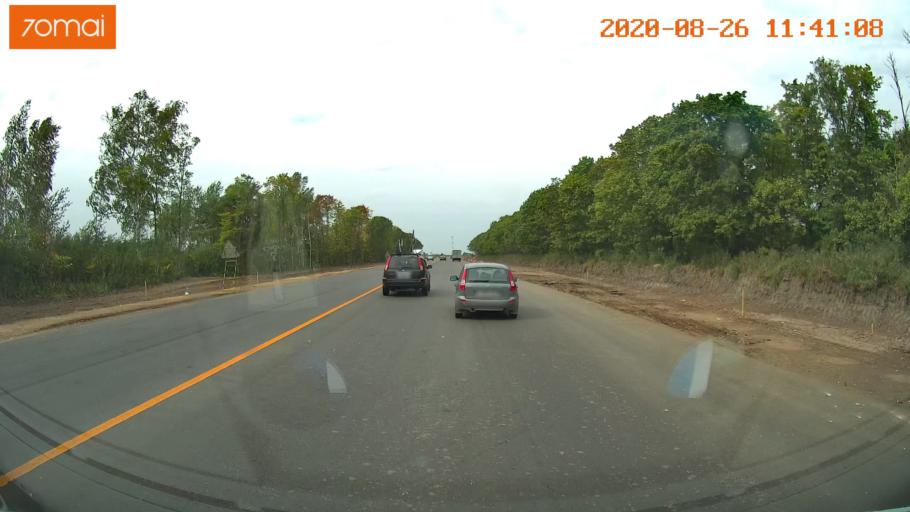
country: RU
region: Rjazan
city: Shilovo
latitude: 54.2950
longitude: 40.7165
